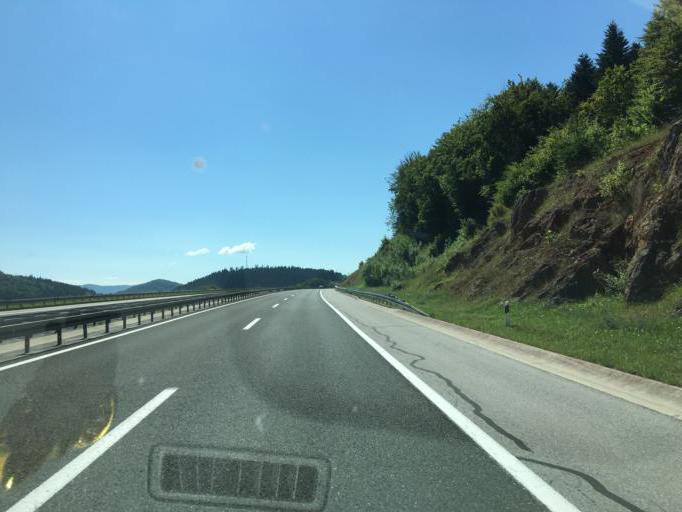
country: HR
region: Licko-Senjska
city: Otocac
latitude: 44.8568
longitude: 15.2204
